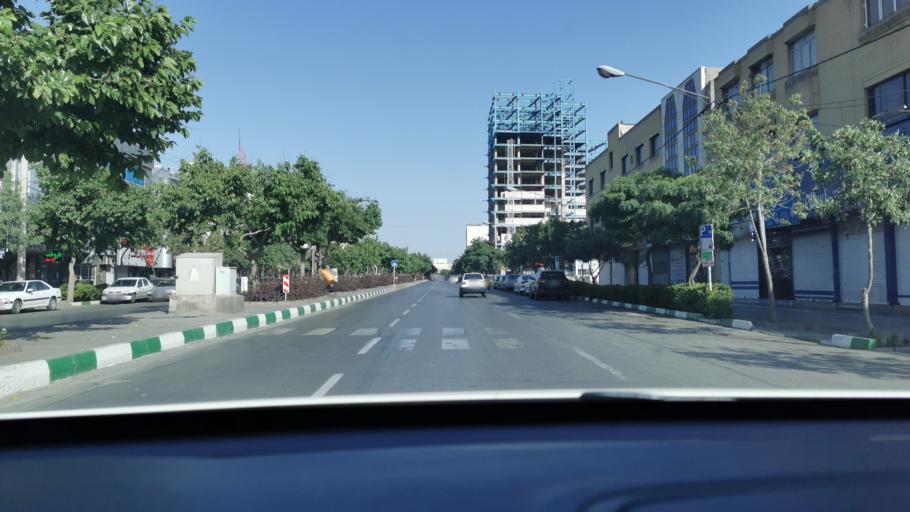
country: IR
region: Razavi Khorasan
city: Mashhad
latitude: 36.3317
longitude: 59.5181
